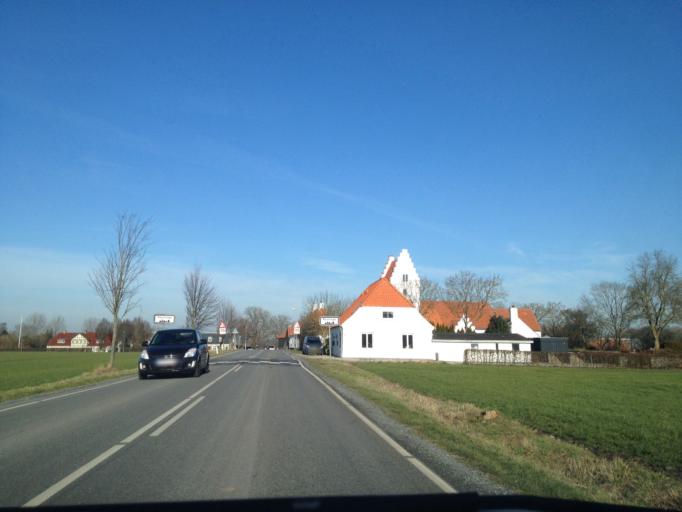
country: DK
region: South Denmark
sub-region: Kerteminde Kommune
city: Kerteminde
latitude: 55.4150
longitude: 10.6605
